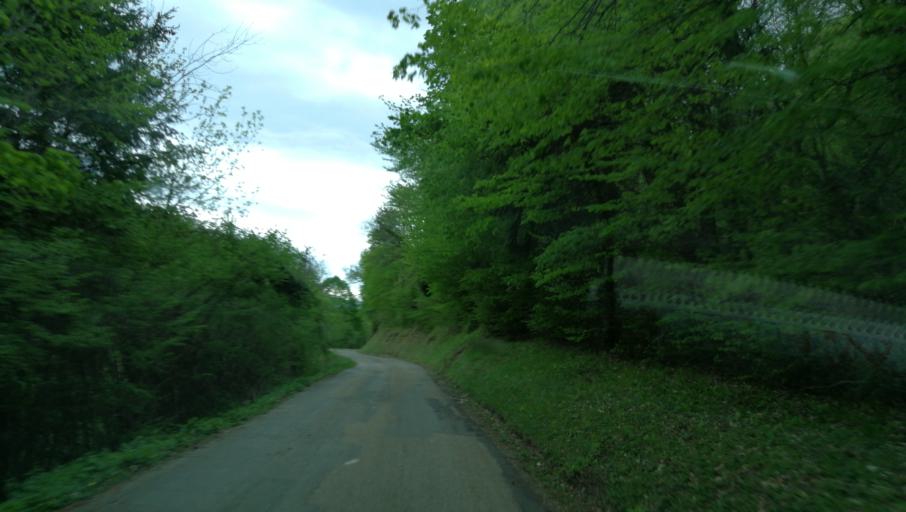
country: FR
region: Rhone-Alpes
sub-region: Departement de la Savoie
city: Brison-Saint-Innocent
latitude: 45.7385
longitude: 5.8386
